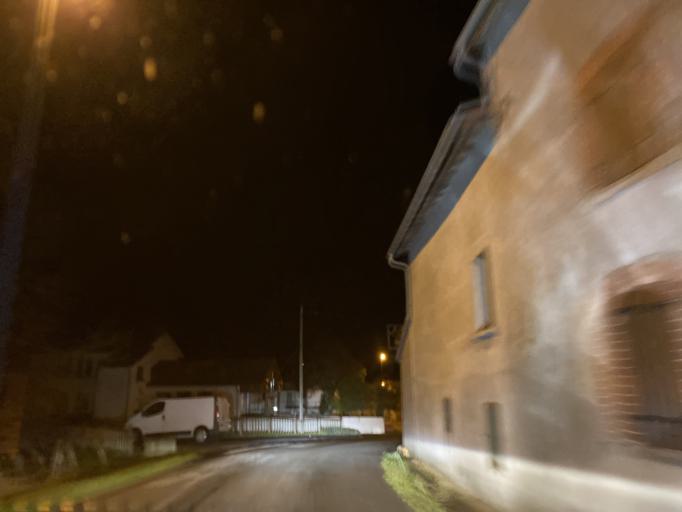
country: FR
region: Auvergne
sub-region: Departement du Puy-de-Dome
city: Cunlhat
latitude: 45.6009
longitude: 3.5083
